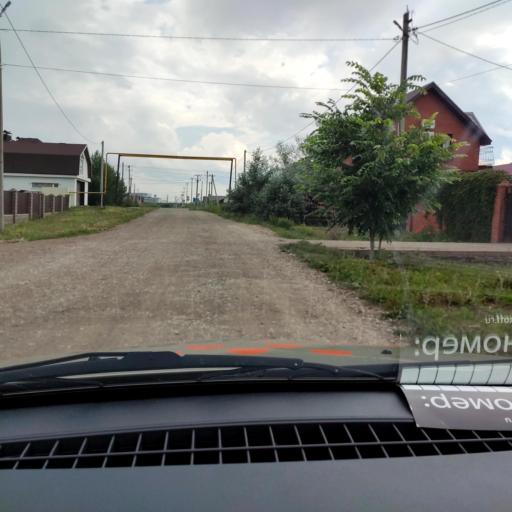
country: RU
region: Bashkortostan
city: Ufa
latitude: 54.6109
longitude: 55.9108
